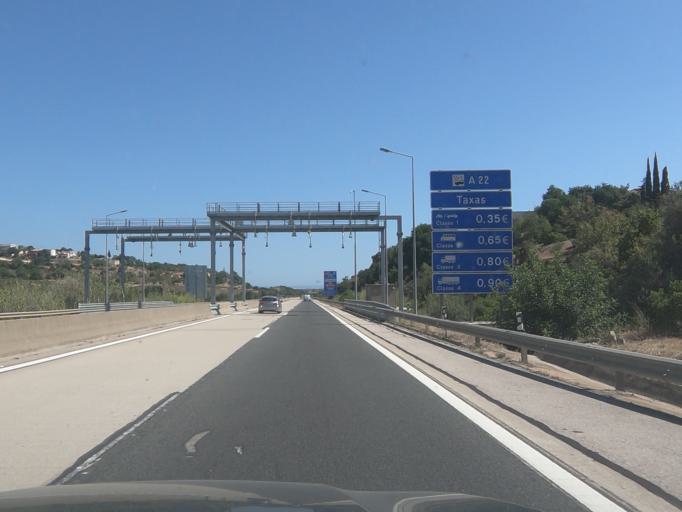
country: PT
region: Faro
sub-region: Loule
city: Almancil
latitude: 37.1078
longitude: -8.0176
